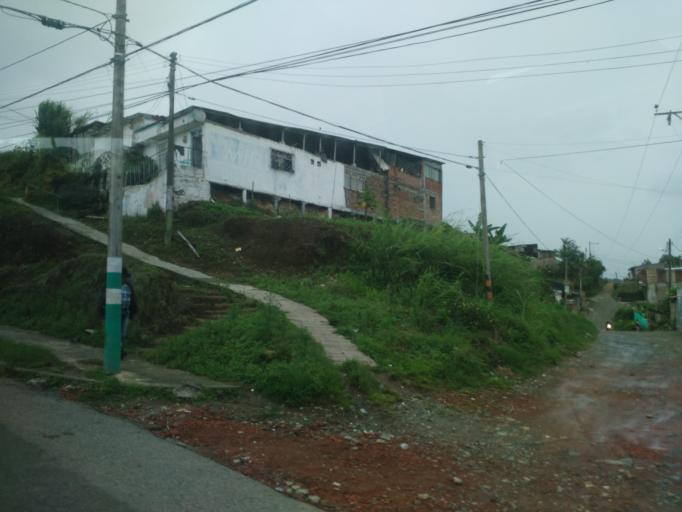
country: CO
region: Valle del Cauca
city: Sevilla
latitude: 4.2668
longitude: -75.9283
